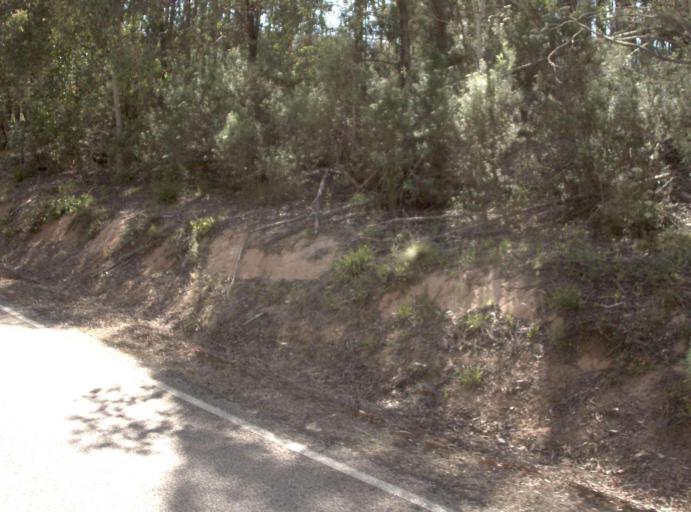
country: AU
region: New South Wales
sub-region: Bombala
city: Bombala
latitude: -37.1600
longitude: 148.7215
